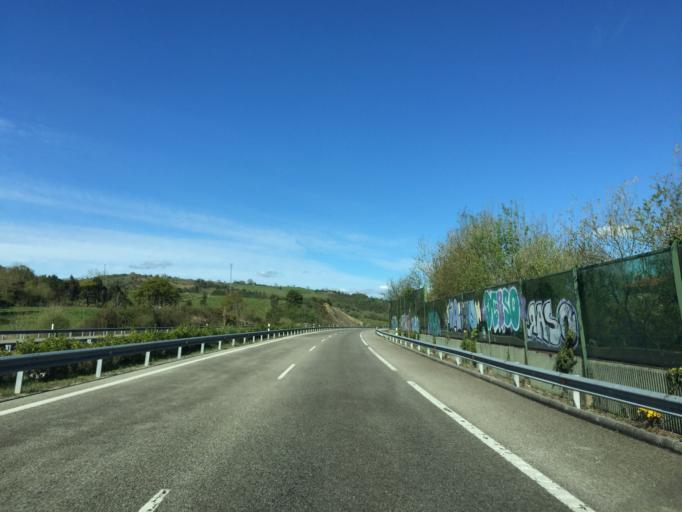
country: ES
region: Asturias
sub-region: Province of Asturias
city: Castandiello
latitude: 43.3532
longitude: -5.9321
